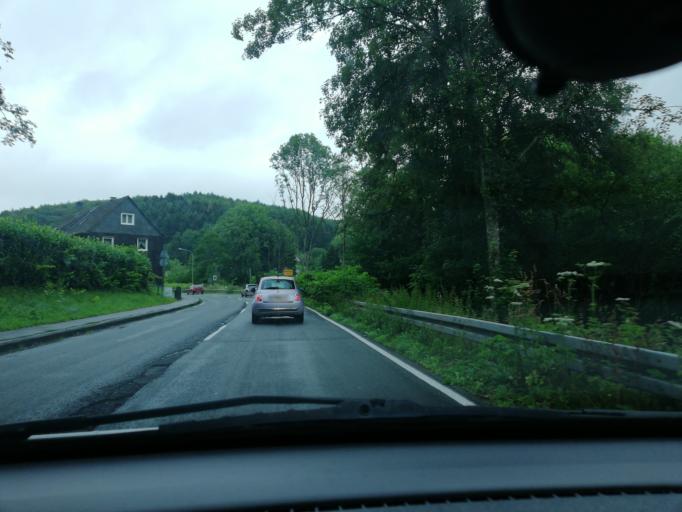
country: DE
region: North Rhine-Westphalia
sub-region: Regierungsbezirk Dusseldorf
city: Remscheid
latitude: 51.2034
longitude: 7.2146
